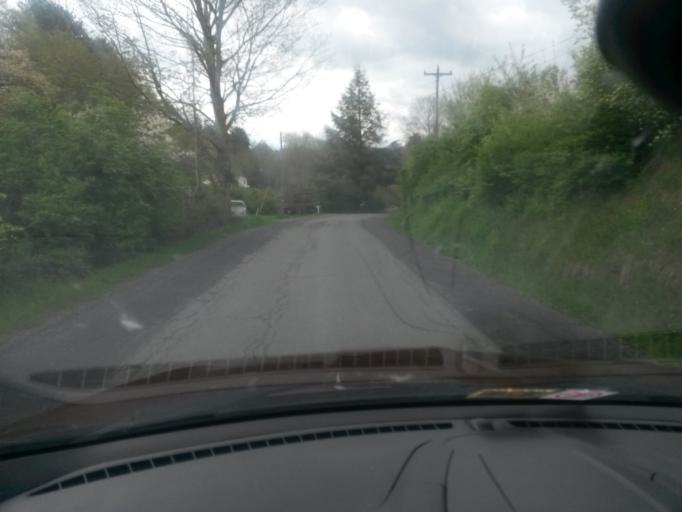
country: US
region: West Virginia
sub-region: Greenbrier County
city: Lewisburg
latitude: 37.9386
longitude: -80.4187
